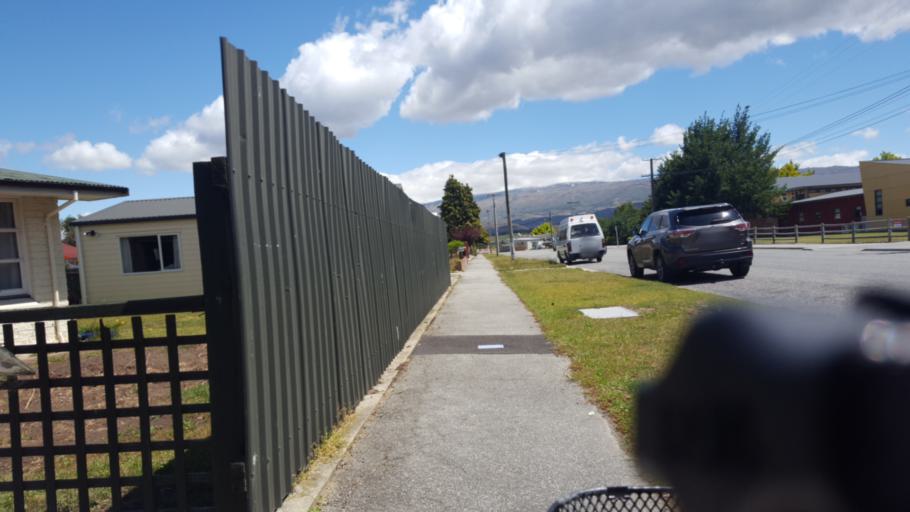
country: NZ
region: Otago
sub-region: Queenstown-Lakes District
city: Wanaka
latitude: -45.2457
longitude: 169.3884
